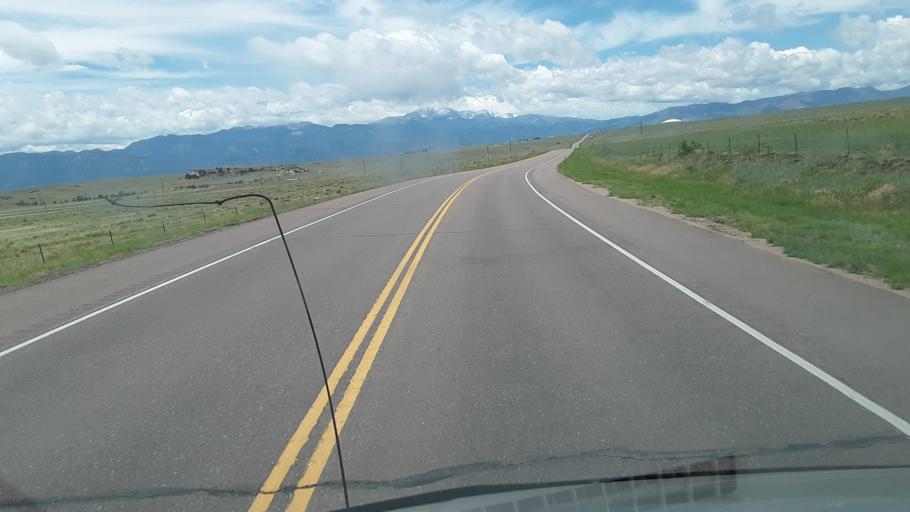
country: US
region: Colorado
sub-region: El Paso County
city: Cimarron Hills
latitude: 38.8350
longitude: -104.6437
